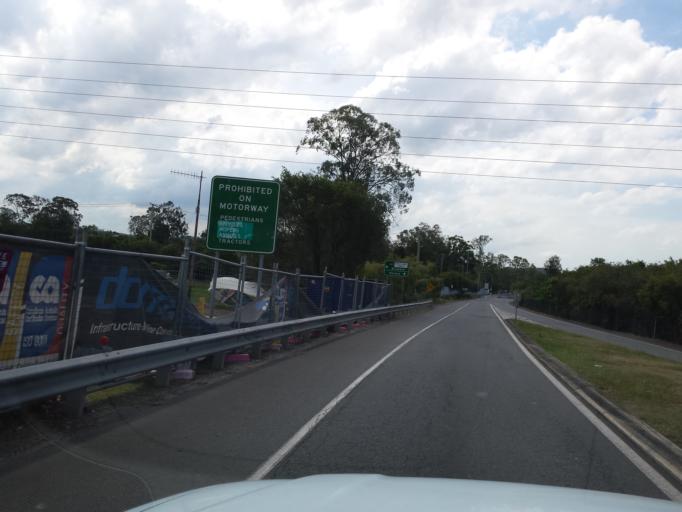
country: AU
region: Queensland
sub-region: Gold Coast
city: Nerang
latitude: -28.0053
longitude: 153.3406
